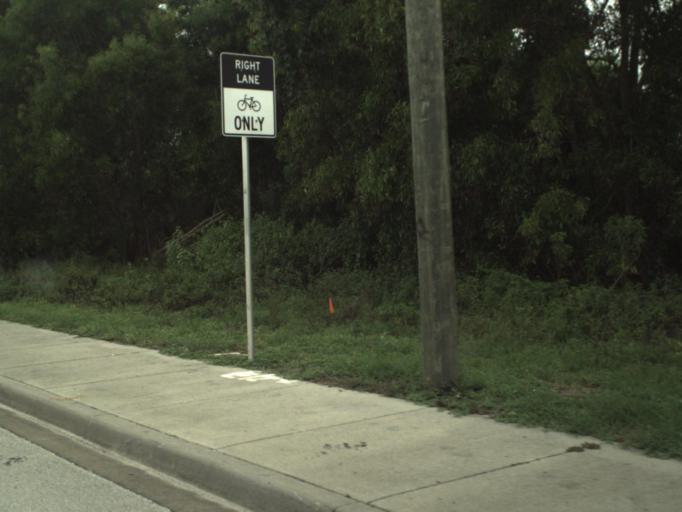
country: US
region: Florida
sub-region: Palm Beach County
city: Mangonia Park
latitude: 26.7546
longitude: -80.1090
